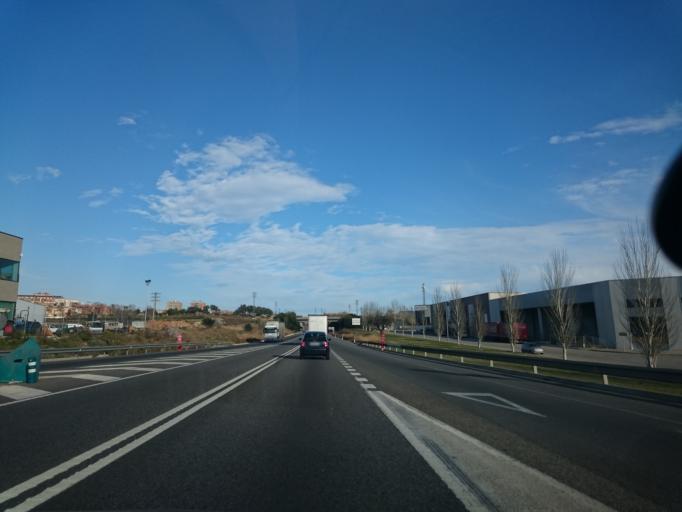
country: ES
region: Catalonia
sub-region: Provincia de Barcelona
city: Vilafranca del Penedes
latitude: 41.3342
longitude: 1.6876
